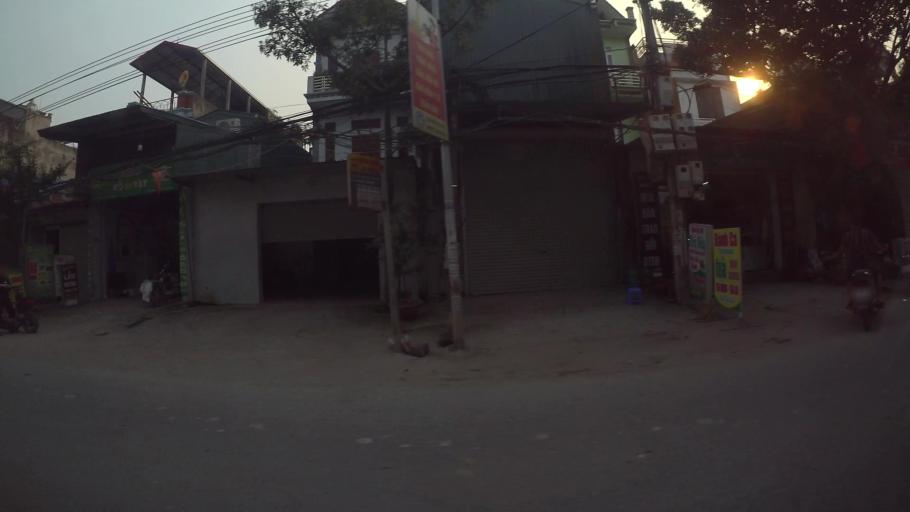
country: VN
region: Ha Noi
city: Kim Bai
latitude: 20.8705
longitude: 105.8058
